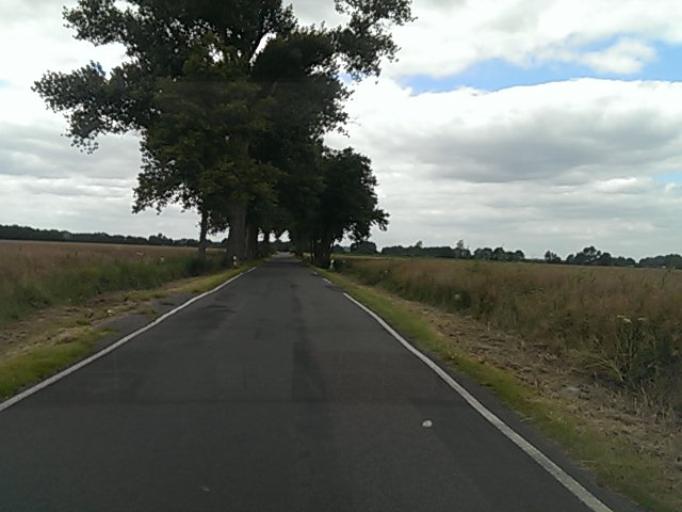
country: DE
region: Brandenburg
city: Linthe
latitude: 52.1564
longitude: 12.8166
